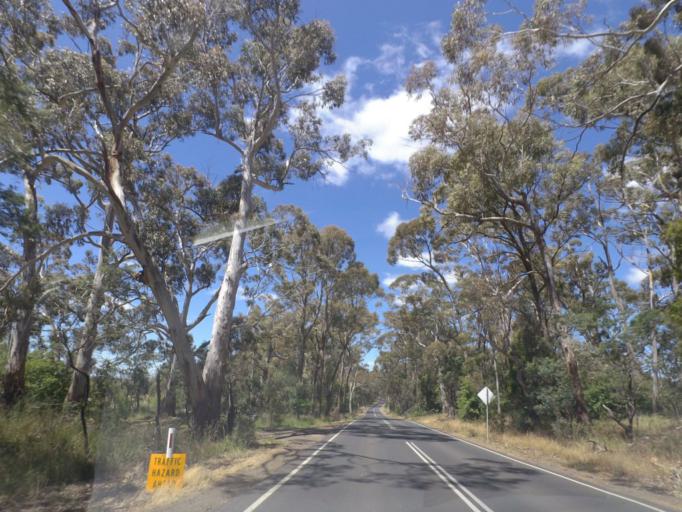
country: AU
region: Victoria
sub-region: Mount Alexander
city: Castlemaine
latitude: -37.2887
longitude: 144.2714
